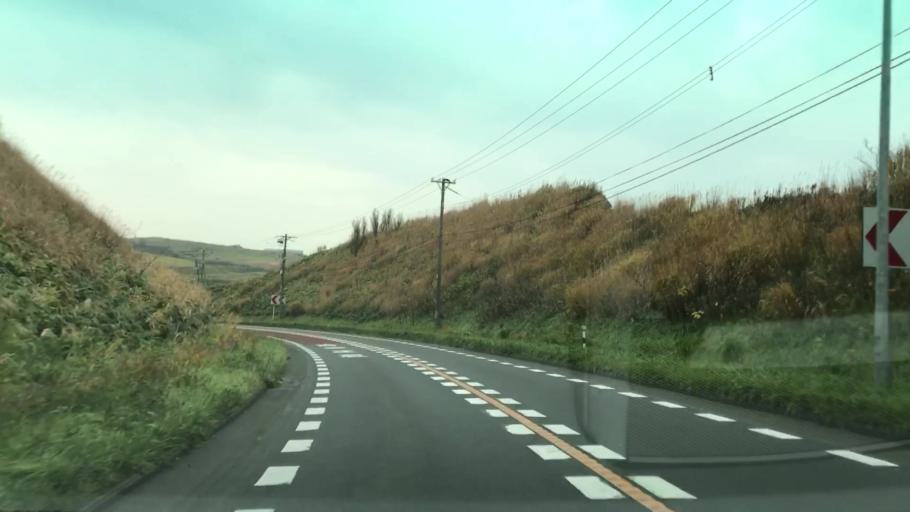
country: JP
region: Hokkaido
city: Ishikari
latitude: 43.3596
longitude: 141.4292
